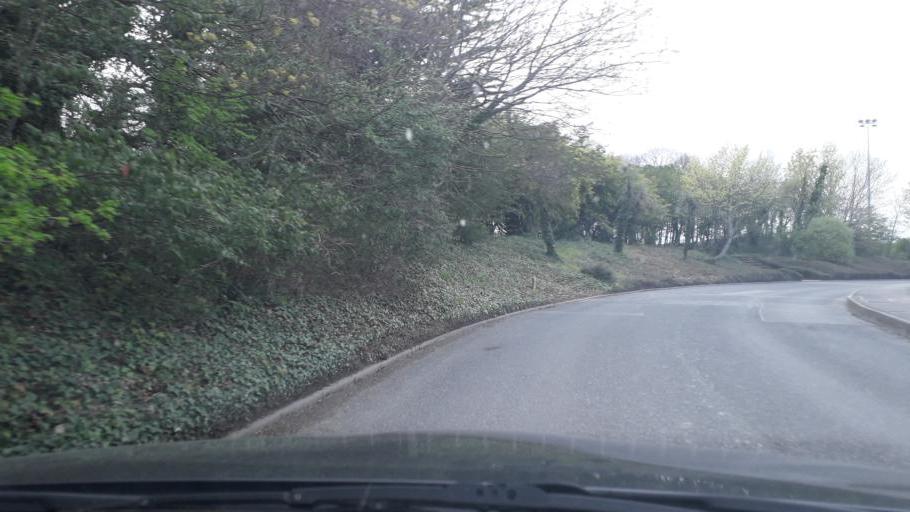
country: IE
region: Leinster
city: Donnybrook
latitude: 53.3059
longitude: -6.2255
